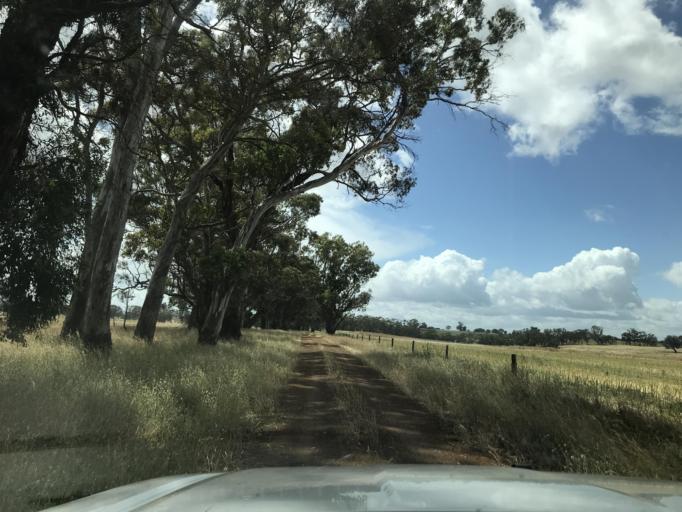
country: AU
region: South Australia
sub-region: Wattle Range
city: Penola
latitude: -37.1847
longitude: 141.4761
